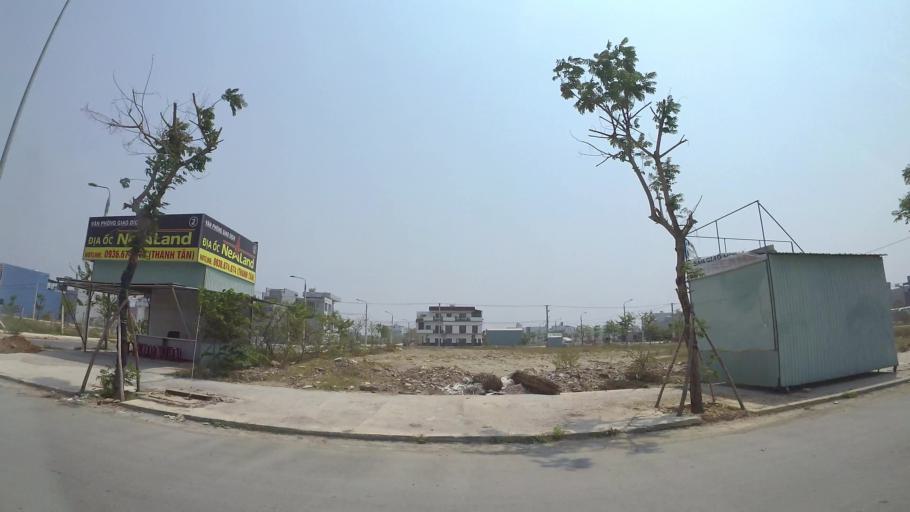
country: VN
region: Da Nang
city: Cam Le
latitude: 16.0126
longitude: 108.2254
